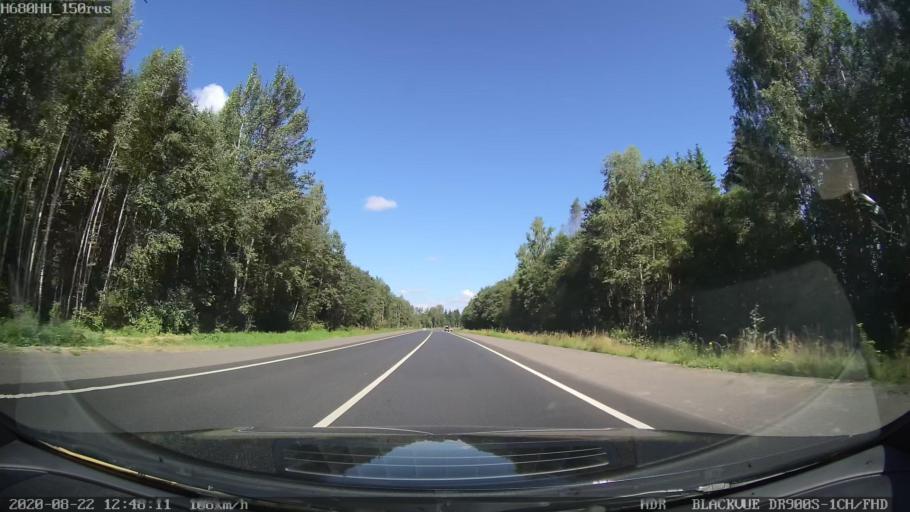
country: RU
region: Tverskaya
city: Rameshki
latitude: 57.4363
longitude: 36.1820
